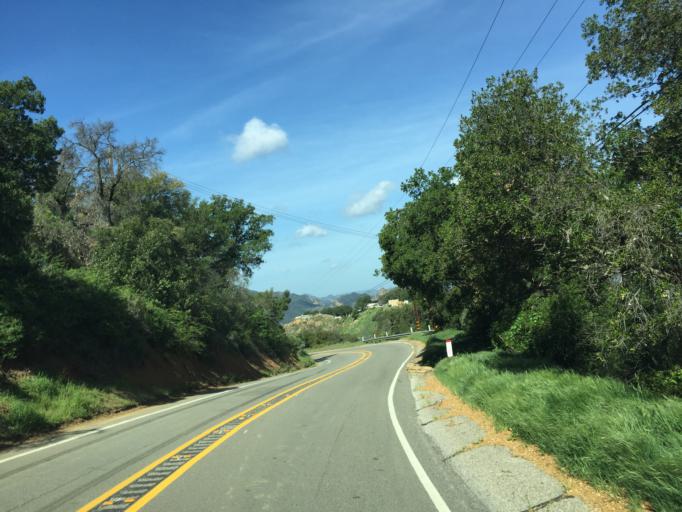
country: US
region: California
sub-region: Los Angeles County
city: Malibu Beach
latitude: 34.0664
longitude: -118.6815
